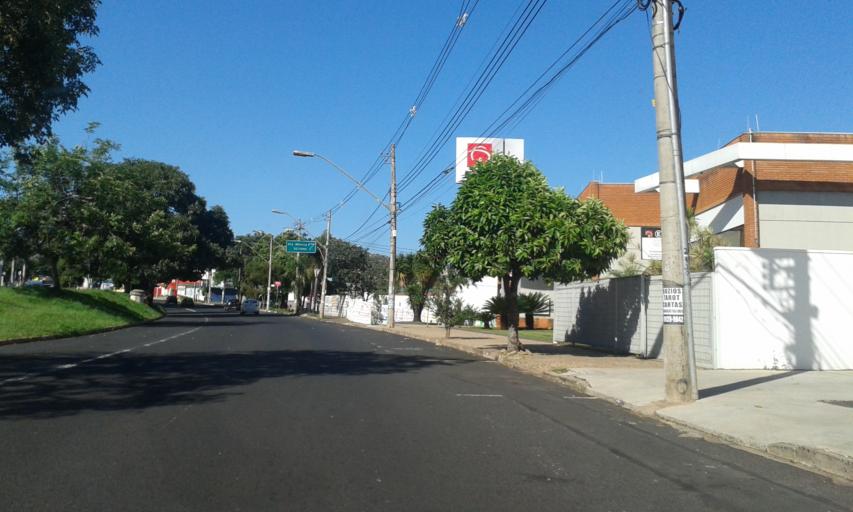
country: BR
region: Minas Gerais
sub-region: Uberlandia
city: Uberlandia
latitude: -18.9200
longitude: -48.2623
